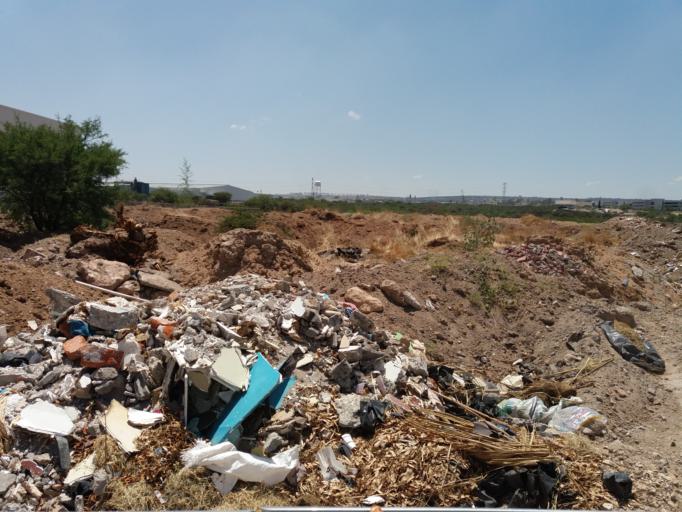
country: MX
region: Aguascalientes
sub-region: Aguascalientes
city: San Sebastian [Fraccionamiento]
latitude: 21.7958
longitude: -102.2981
